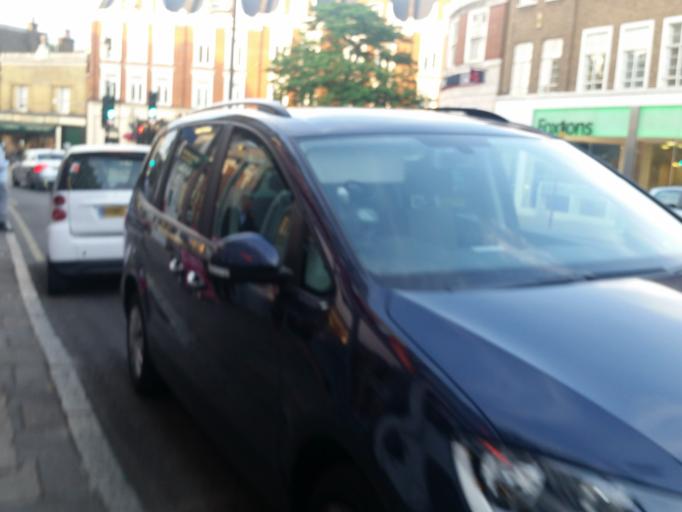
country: GB
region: England
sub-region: Greater London
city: Crouch End
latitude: 51.5780
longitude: -0.1244
